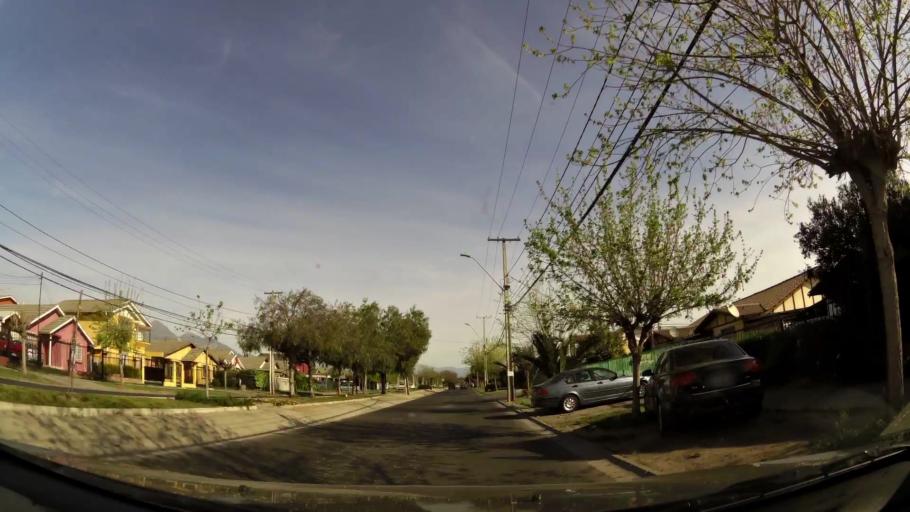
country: CL
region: Santiago Metropolitan
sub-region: Provincia de Cordillera
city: Puente Alto
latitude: -33.5819
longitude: -70.5636
